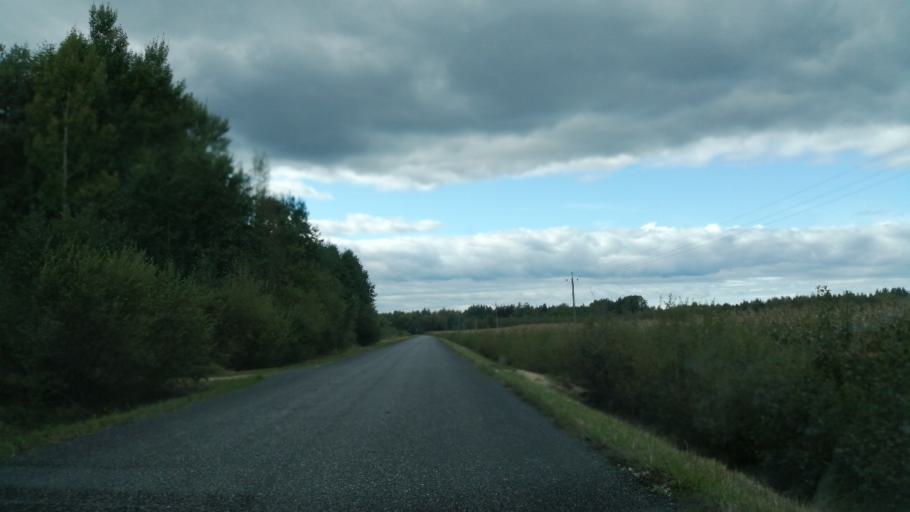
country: EE
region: Jaervamaa
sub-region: Tueri vald
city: Tueri
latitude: 58.8054
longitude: 25.4646
